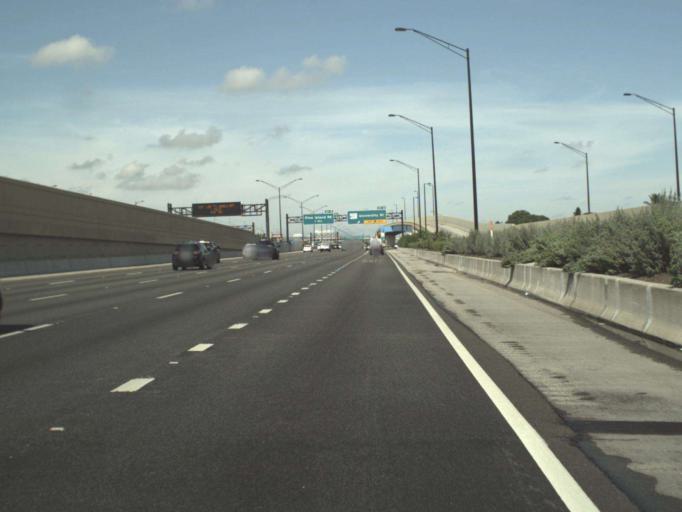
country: US
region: Florida
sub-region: Broward County
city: Broadview Park
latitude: 26.0949
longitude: -80.2320
